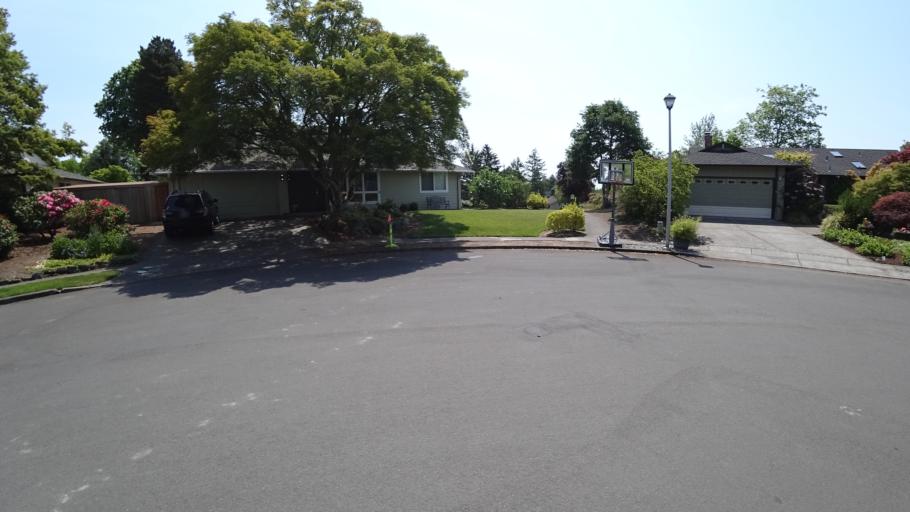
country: US
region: Oregon
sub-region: Washington County
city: Oak Hills
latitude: 45.5399
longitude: -122.8309
